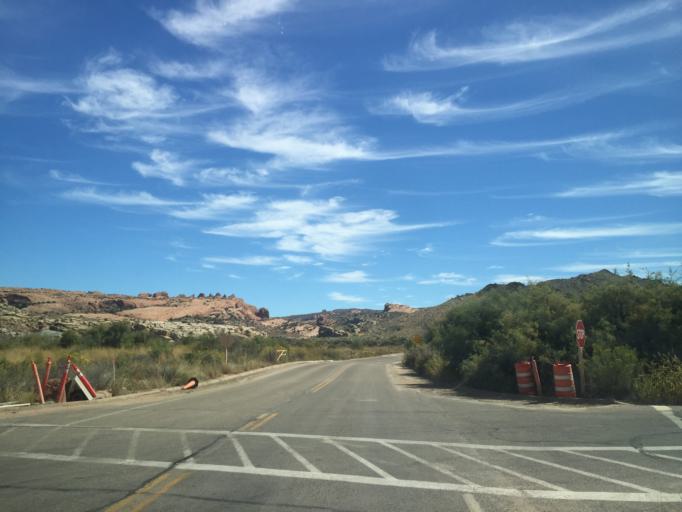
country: US
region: Utah
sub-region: Grand County
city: Moab
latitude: 38.7351
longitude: -109.5204
